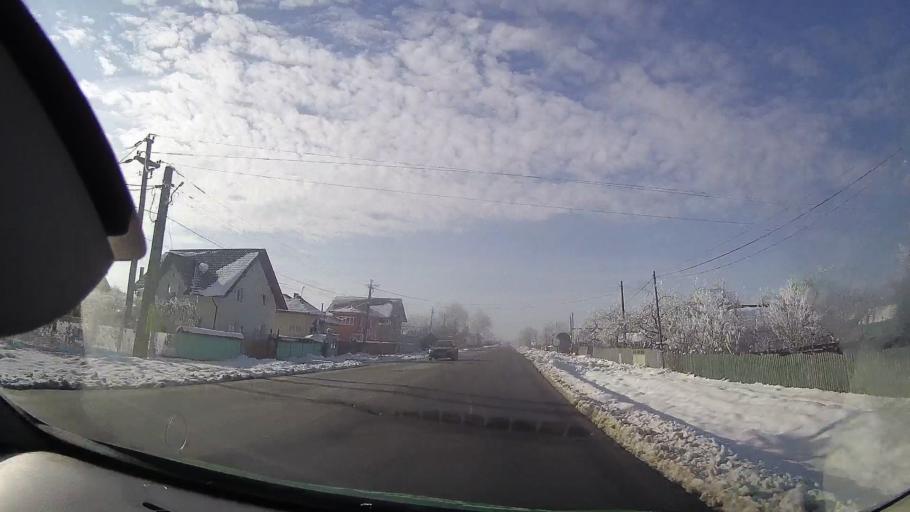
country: RO
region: Neamt
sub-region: Comuna Timisesti
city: Timisesti
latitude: 47.2349
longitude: 26.5339
